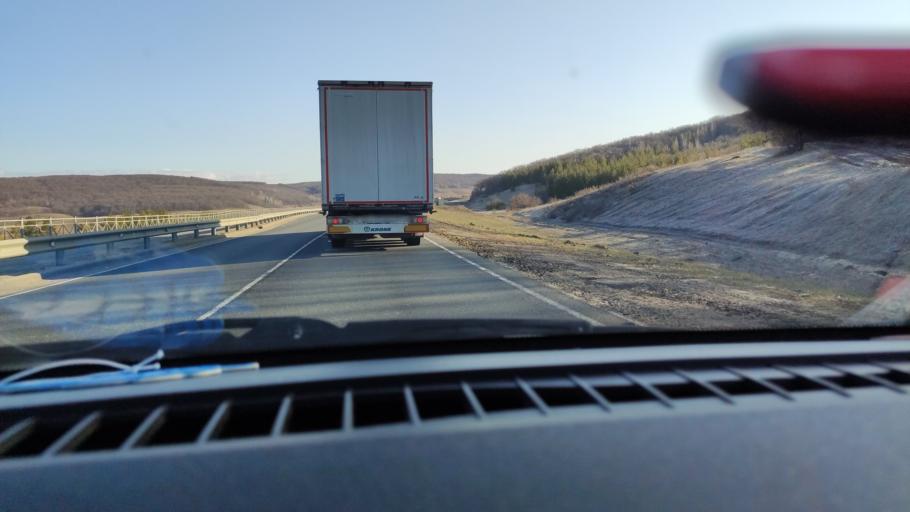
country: RU
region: Saratov
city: Alekseyevka
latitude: 52.3898
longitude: 47.9762
